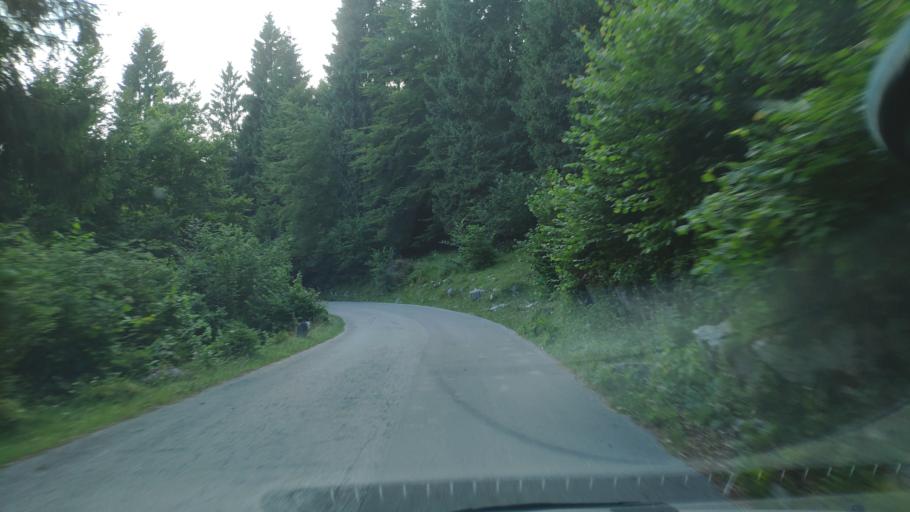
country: IT
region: Veneto
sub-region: Provincia di Vicenza
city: Calvene
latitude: 45.8003
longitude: 11.5133
